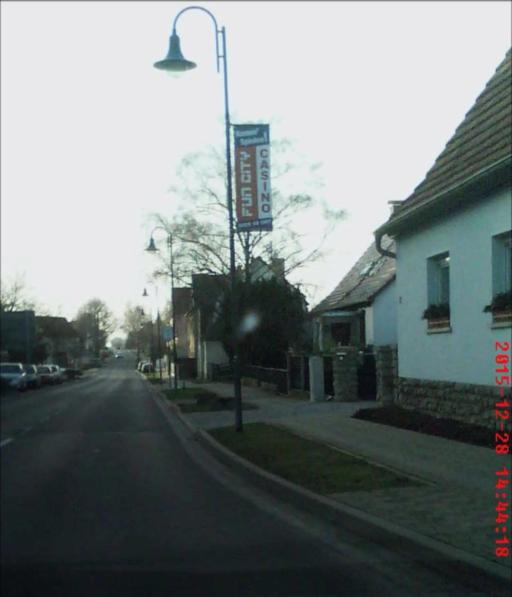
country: DE
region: Thuringia
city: Berlstedt
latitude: 51.0627
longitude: 11.2491
